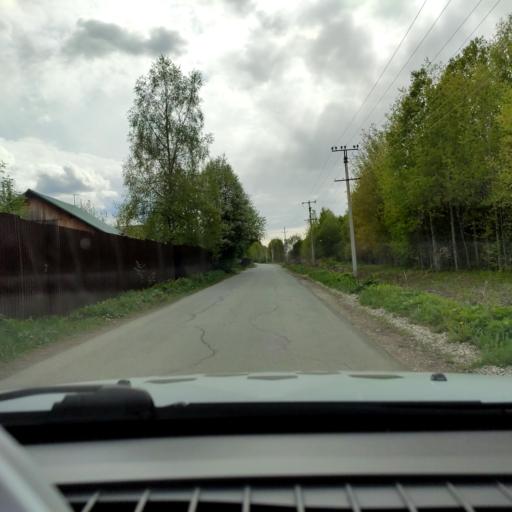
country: RU
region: Perm
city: Novyye Lyady
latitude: 58.0464
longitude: 56.6392
